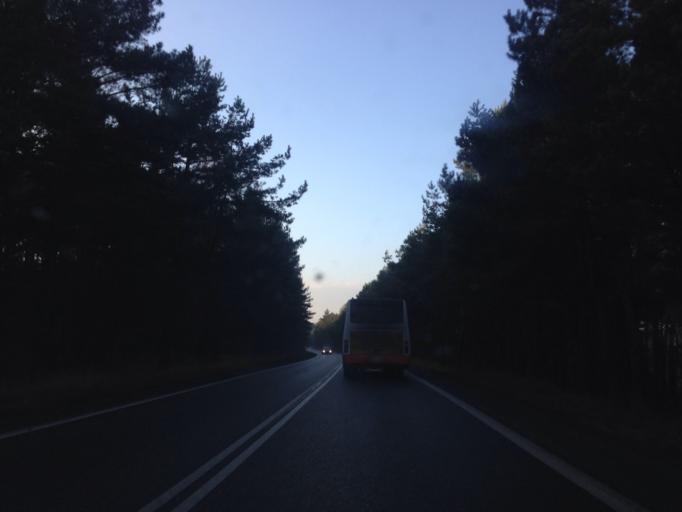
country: PL
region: Kujawsko-Pomorskie
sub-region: Bydgoszcz
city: Fordon
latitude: 53.0739
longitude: 18.1482
